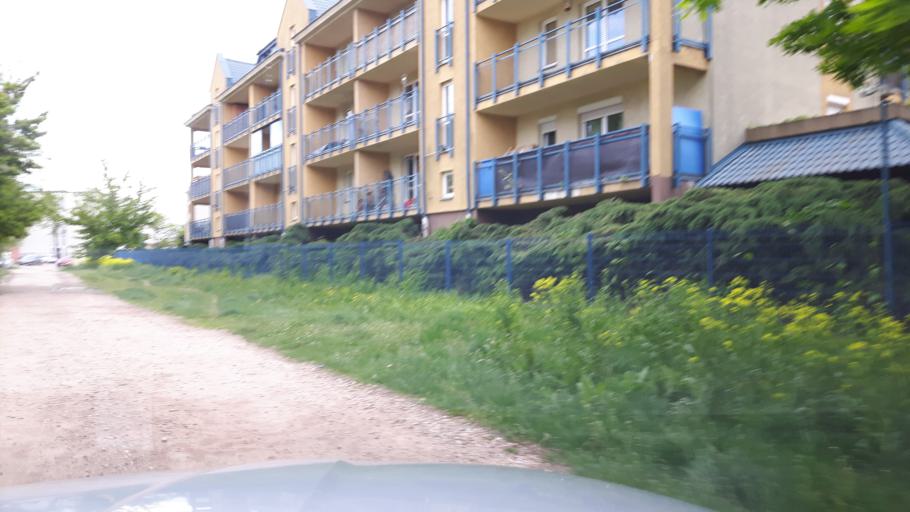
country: PL
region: Masovian Voivodeship
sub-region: Powiat wolominski
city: Zabki
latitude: 52.2893
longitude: 21.0838
